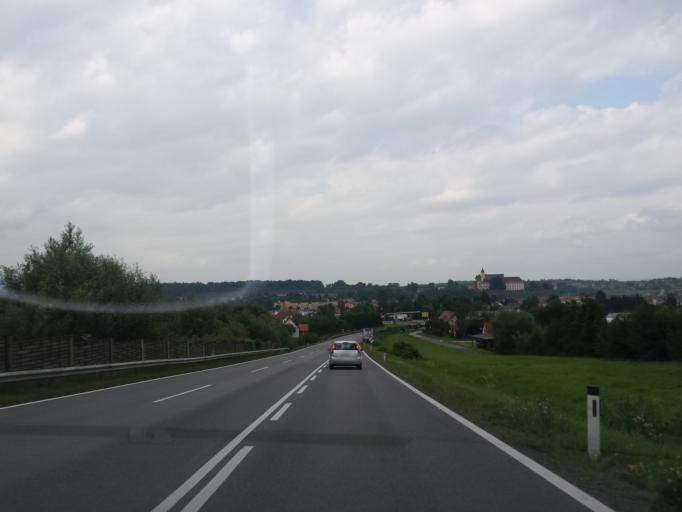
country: AT
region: Styria
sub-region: Politischer Bezirk Deutschlandsberg
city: Stainz
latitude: 46.8842
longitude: 15.2588
